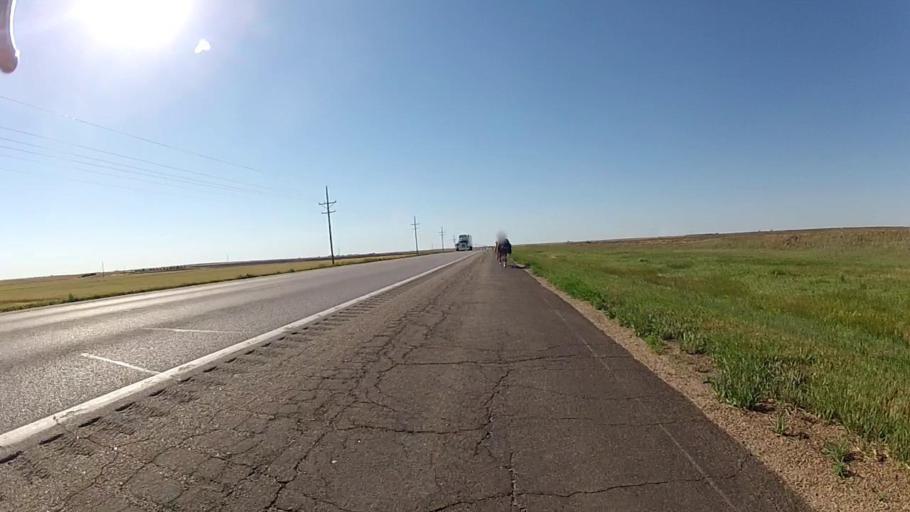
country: US
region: Kansas
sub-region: Ford County
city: Dodge City
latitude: 37.6052
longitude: -99.7072
